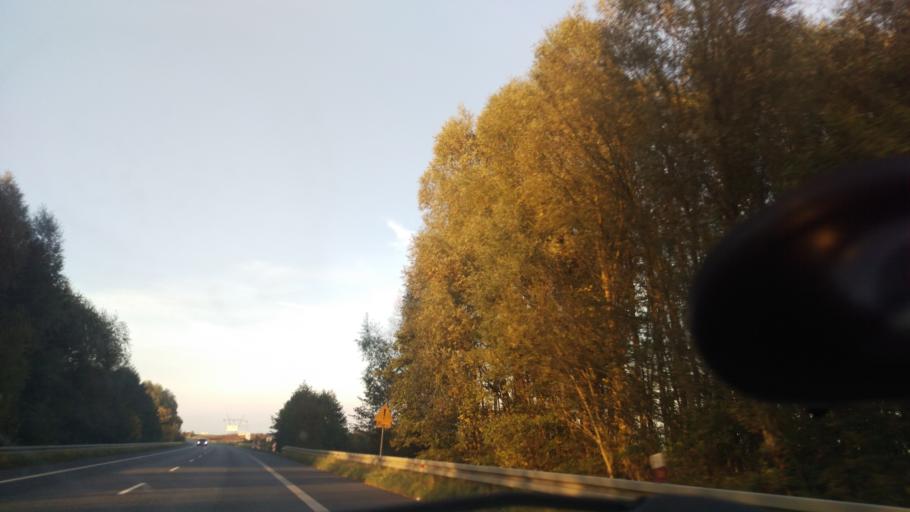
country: PL
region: West Pomeranian Voivodeship
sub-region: Powiat gryfinski
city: Stare Czarnowo
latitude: 53.2844
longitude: 14.7866
